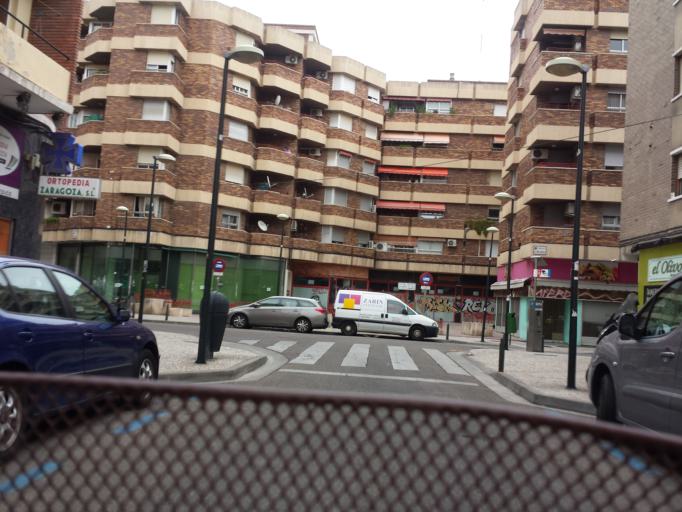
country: ES
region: Aragon
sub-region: Provincia de Zaragoza
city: Delicias
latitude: 41.6535
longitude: -0.9015
